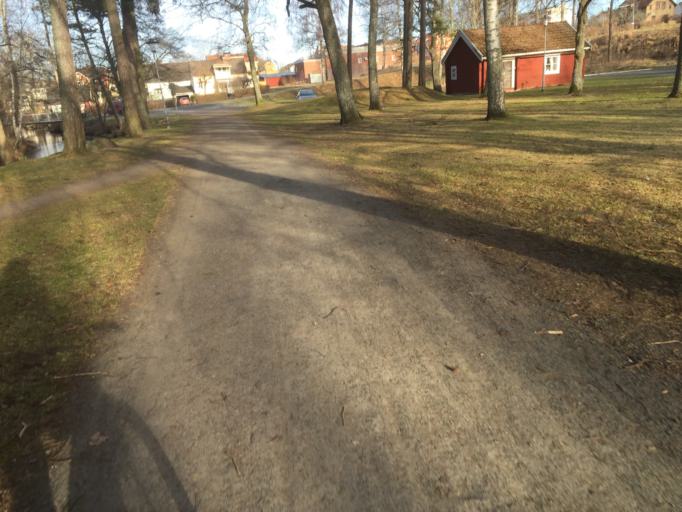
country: SE
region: Joenkoeping
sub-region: Aneby Kommun
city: Aneby
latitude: 57.8360
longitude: 14.8148
